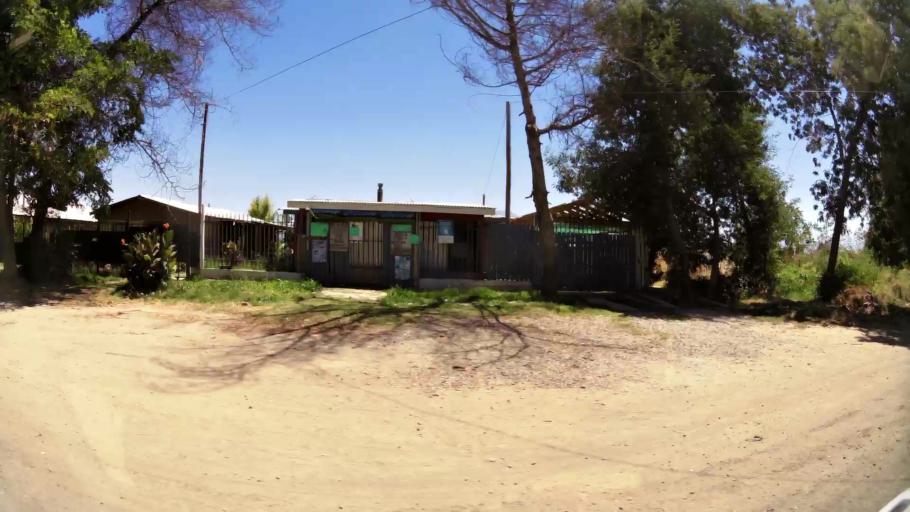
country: CL
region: O'Higgins
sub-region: Provincia de Cachapoal
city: Rancagua
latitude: -34.2206
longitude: -70.7815
